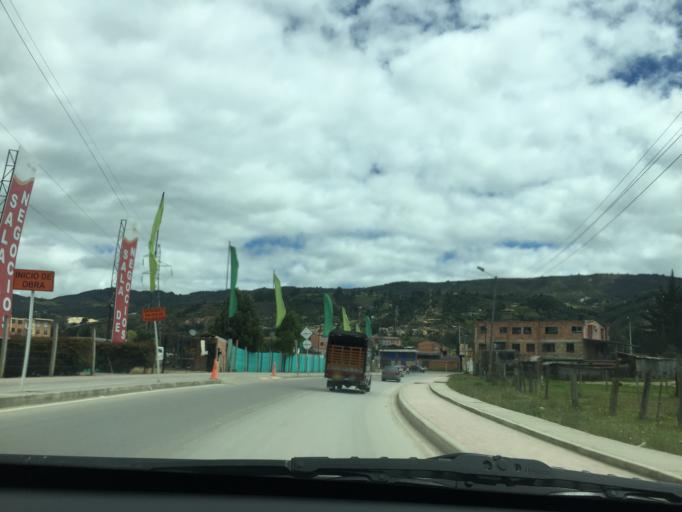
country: CO
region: Cundinamarca
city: Tocancipa
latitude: 4.9627
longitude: -73.9192
